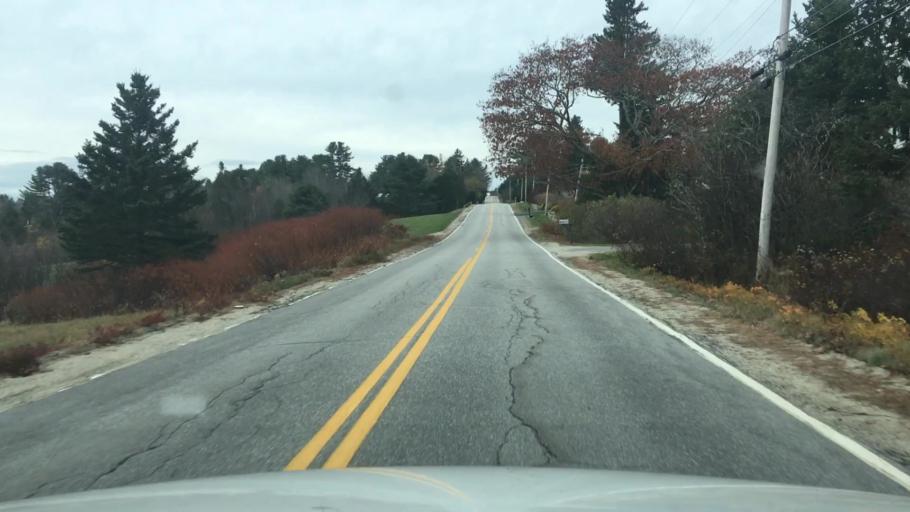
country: US
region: Maine
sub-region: Hancock County
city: Sedgwick
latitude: 44.3485
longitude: -68.5535
